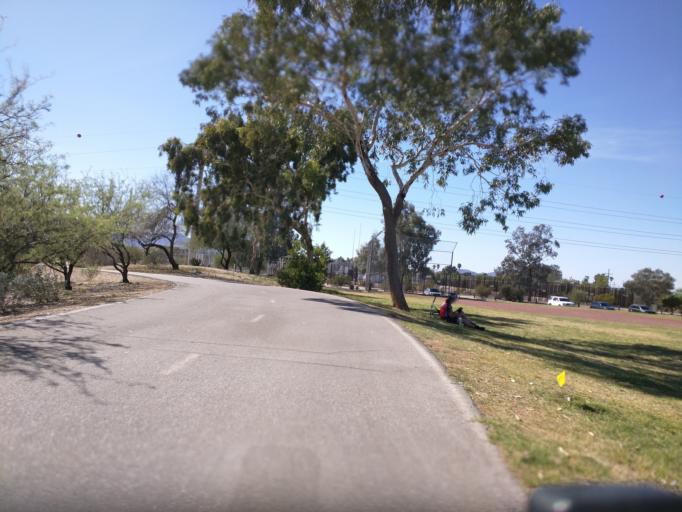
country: US
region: Arizona
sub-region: Pima County
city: Flowing Wells
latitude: 32.2945
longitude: -110.9858
